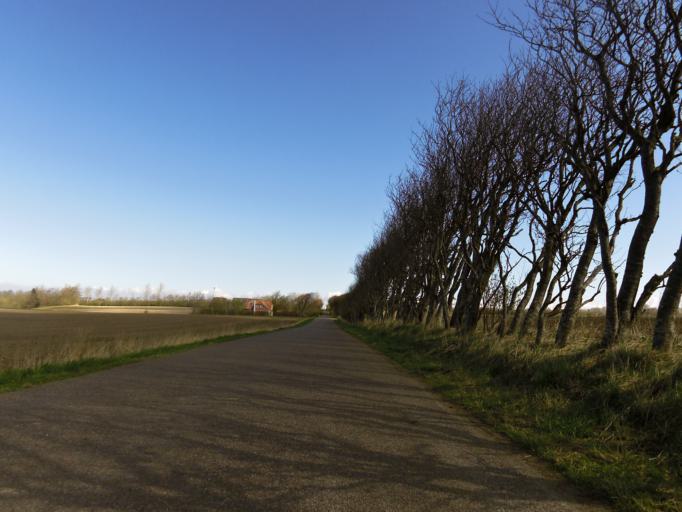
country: DK
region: Central Jutland
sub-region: Holstebro Kommune
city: Vinderup
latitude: 56.4322
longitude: 8.7582
